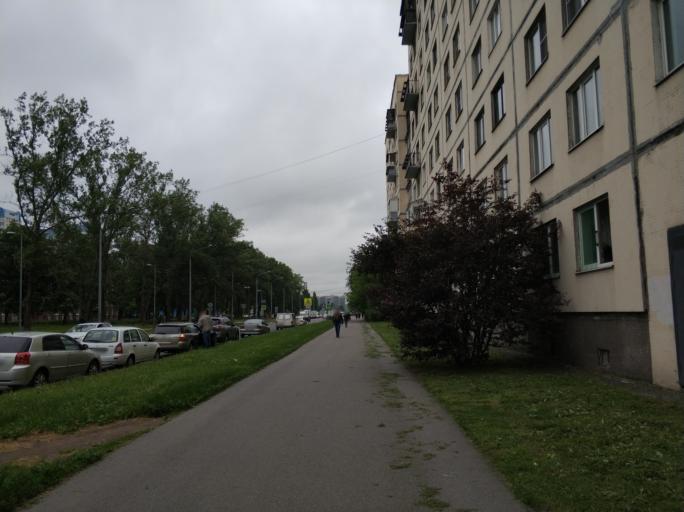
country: RU
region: St.-Petersburg
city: Grazhdanka
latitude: 60.0390
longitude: 30.4131
